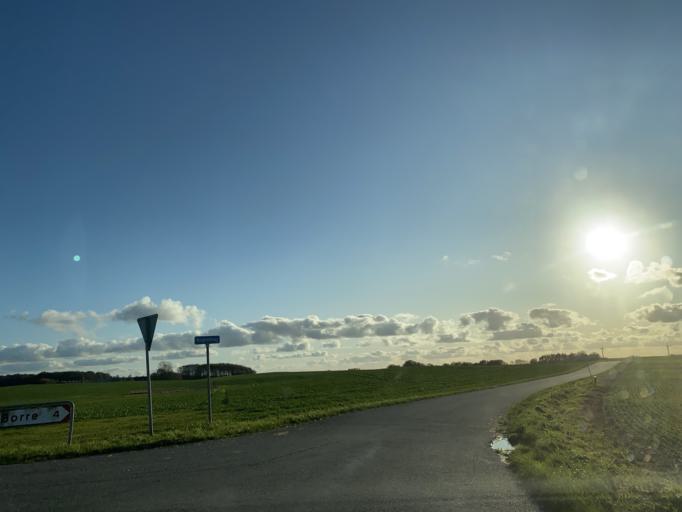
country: DK
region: Central Jutland
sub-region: Viborg Kommune
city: Bjerringbro
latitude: 56.3474
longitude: 9.7180
